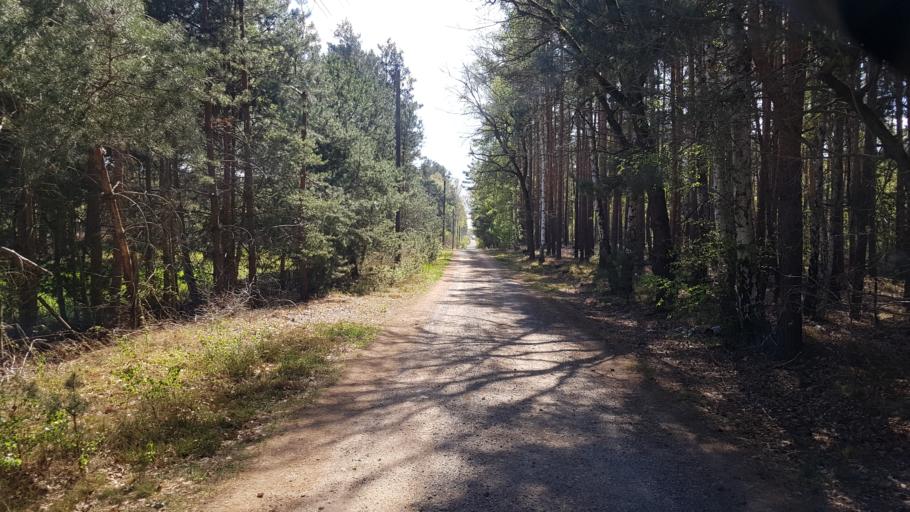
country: DE
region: Brandenburg
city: Crinitz
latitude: 51.7501
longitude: 13.7710
